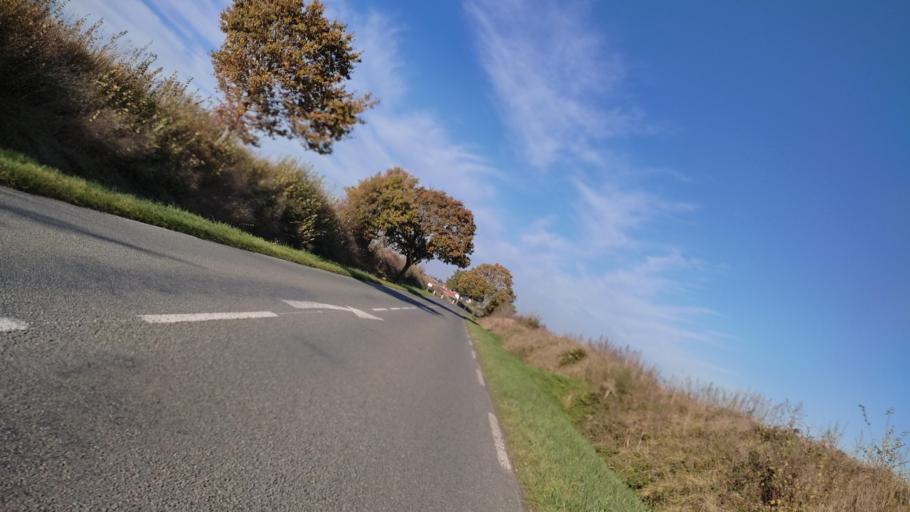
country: FR
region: Nord-Pas-de-Calais
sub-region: Departement du Pas-de-Calais
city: Agny
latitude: 50.2598
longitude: 2.7721
